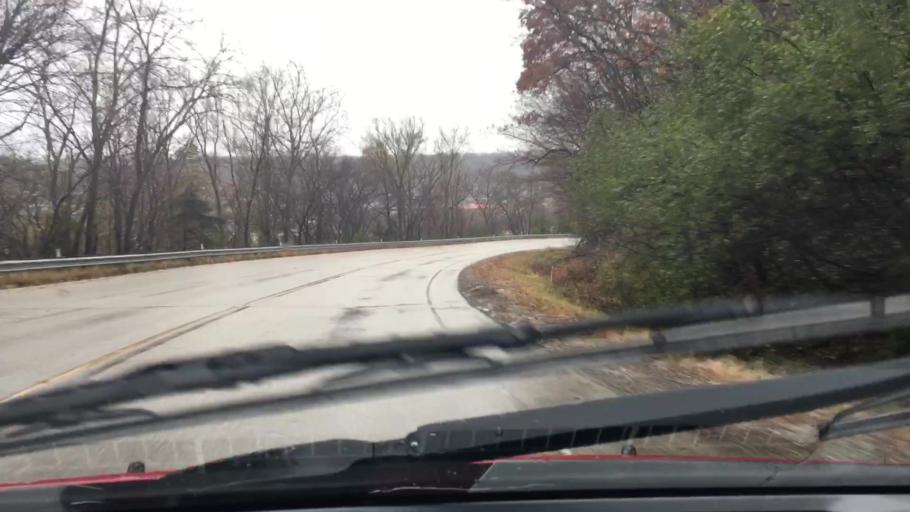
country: US
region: Minnesota
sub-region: Fillmore County
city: Preston
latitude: 43.7257
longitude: -91.9802
